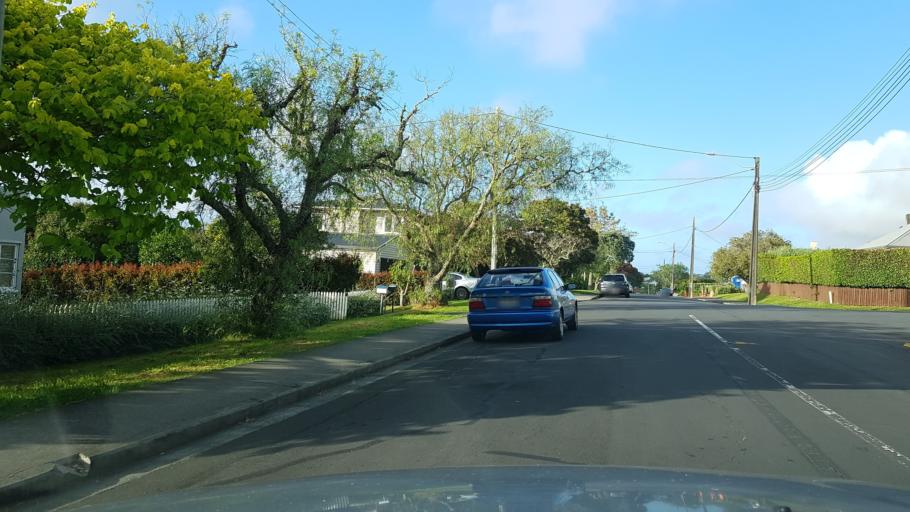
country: NZ
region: Auckland
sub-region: Auckland
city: North Shore
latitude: -36.8167
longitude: 174.7427
